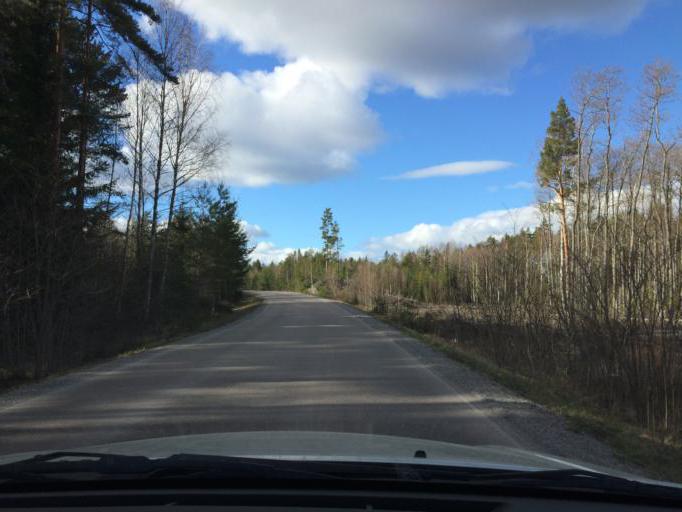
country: SE
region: Soedermanland
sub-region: Eskilstuna Kommun
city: Torshalla
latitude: 59.4236
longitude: 16.4338
